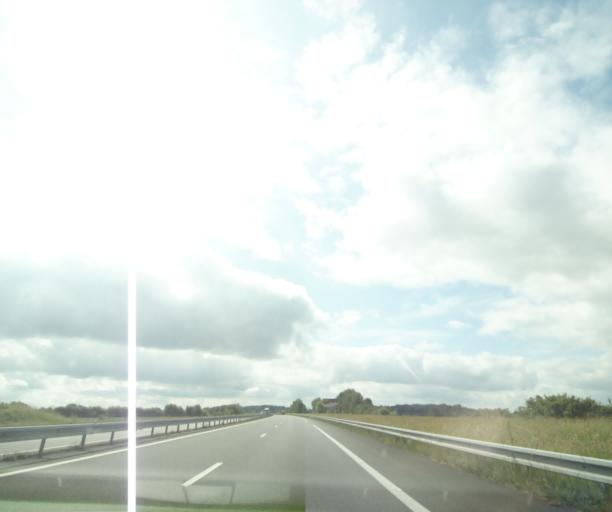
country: FR
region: Pays de la Loire
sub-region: Departement de Maine-et-Loire
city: Vivy
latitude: 47.3472
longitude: -0.0711
